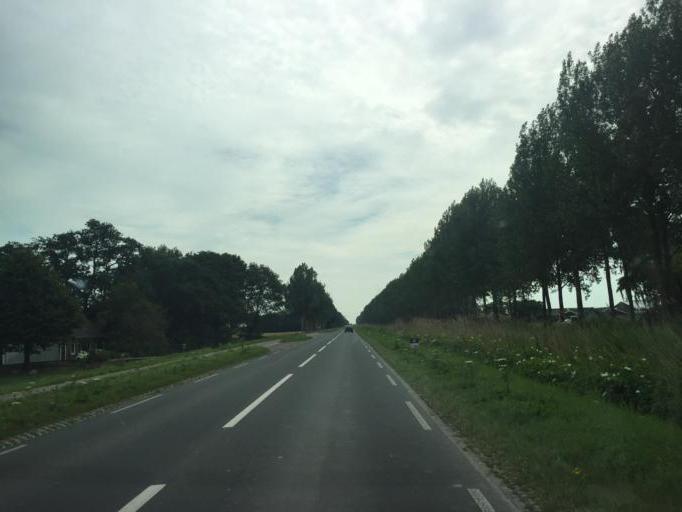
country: NL
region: North Holland
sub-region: Gemeente Heerhugowaard
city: Heerhugowaard
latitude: 52.6090
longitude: 4.8334
